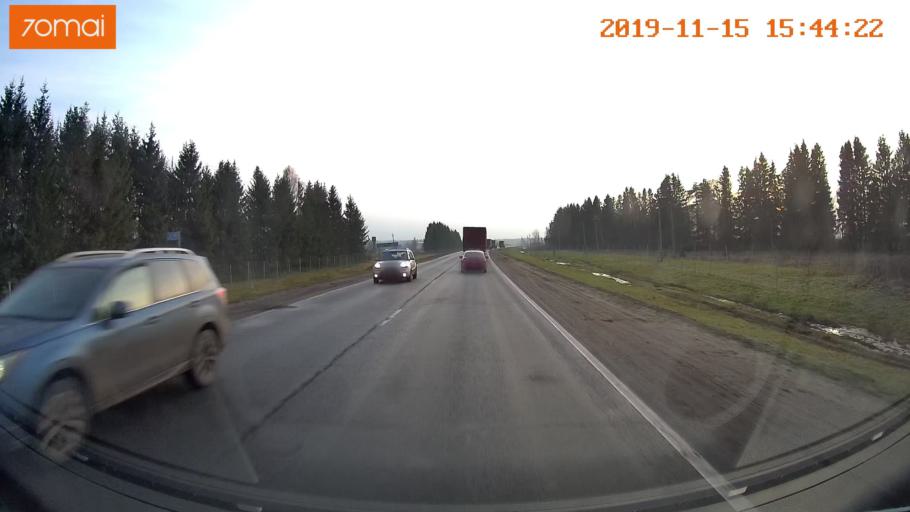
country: RU
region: Jaroslavl
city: Danilov
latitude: 57.9711
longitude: 40.0225
